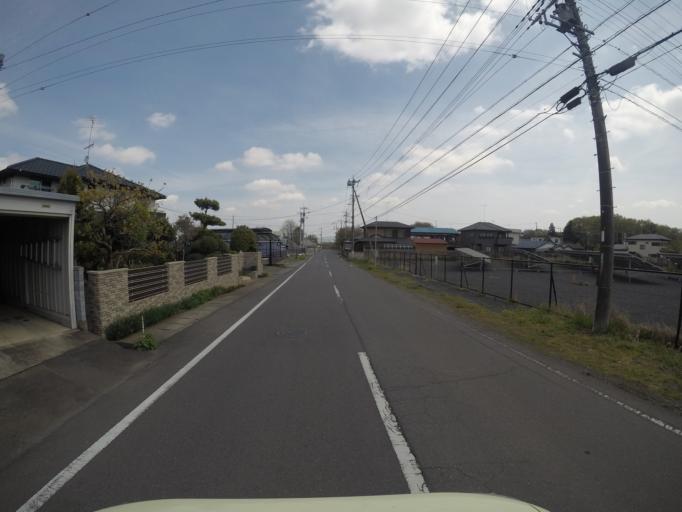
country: JP
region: Ibaraki
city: Shimodate
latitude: 36.2707
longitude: 140.0160
